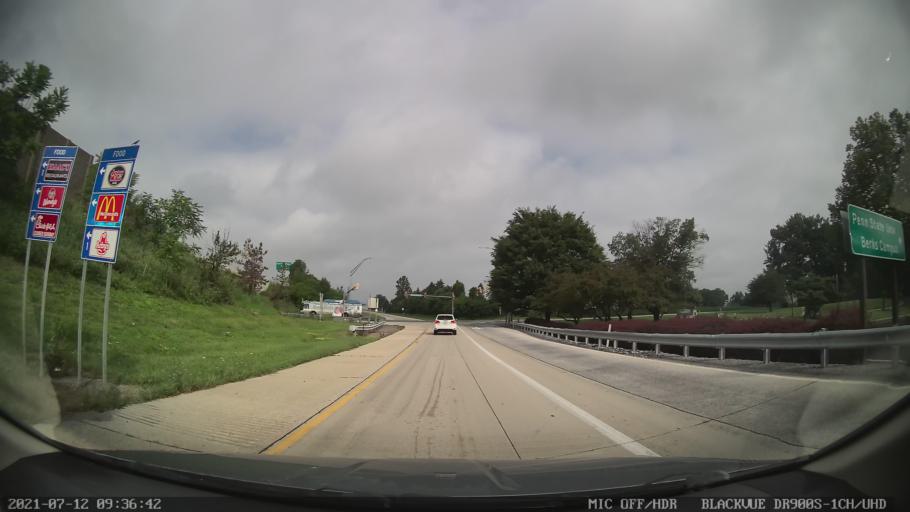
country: US
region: Pennsylvania
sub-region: Berks County
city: Spring Ridge
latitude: 40.3587
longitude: -75.9770
